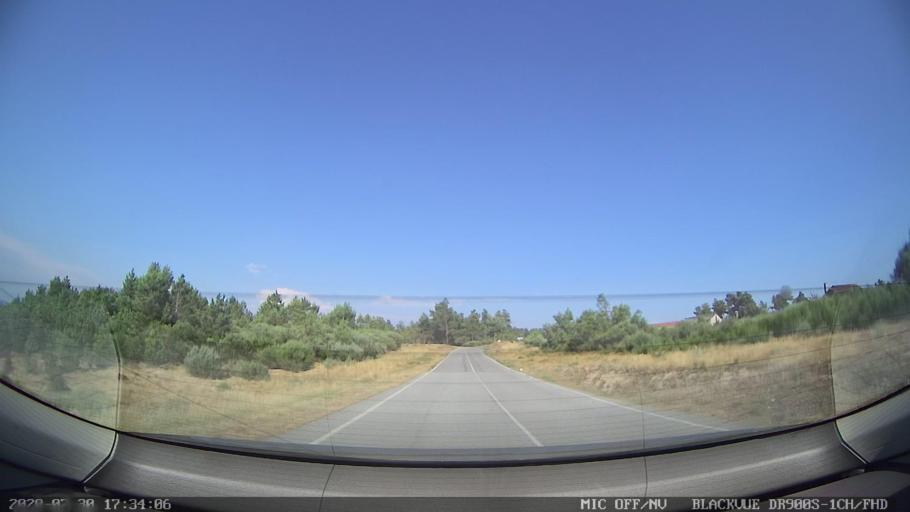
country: PT
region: Vila Real
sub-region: Murca
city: Murca
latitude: 41.3530
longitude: -7.4810
